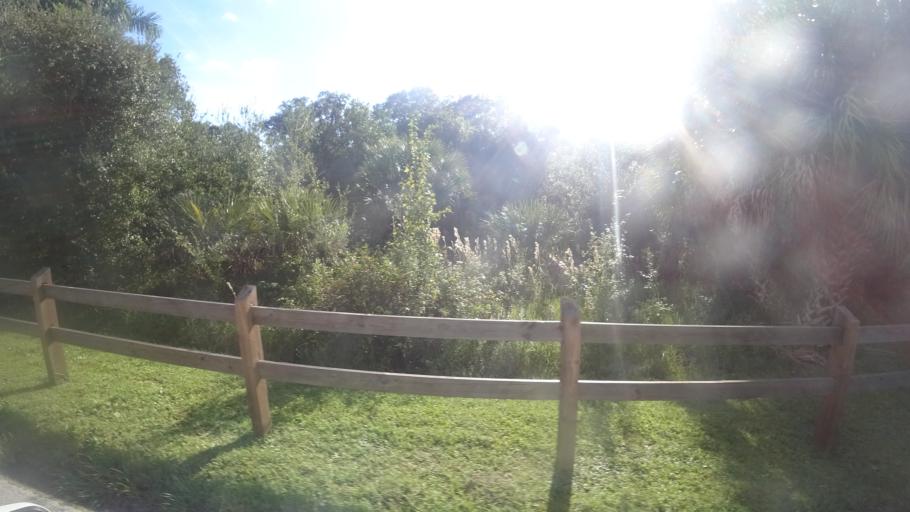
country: US
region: Florida
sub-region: Manatee County
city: West Bradenton
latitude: 27.5310
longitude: -82.6242
